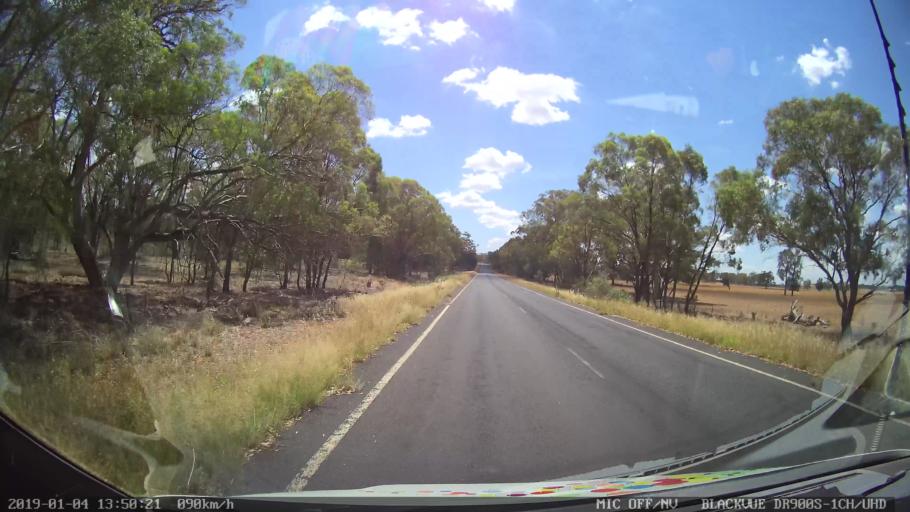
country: AU
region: New South Wales
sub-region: Dubbo Municipality
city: Dubbo
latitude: -32.4209
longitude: 148.5734
